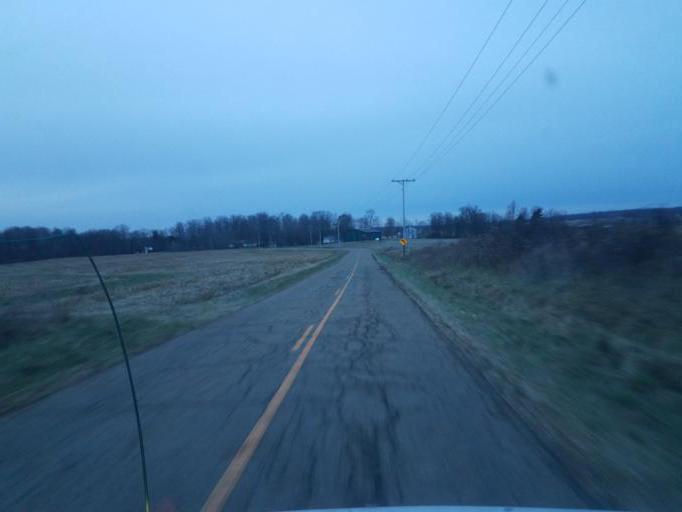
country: US
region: Ohio
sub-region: Licking County
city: Utica
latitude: 40.2948
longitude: -82.4328
